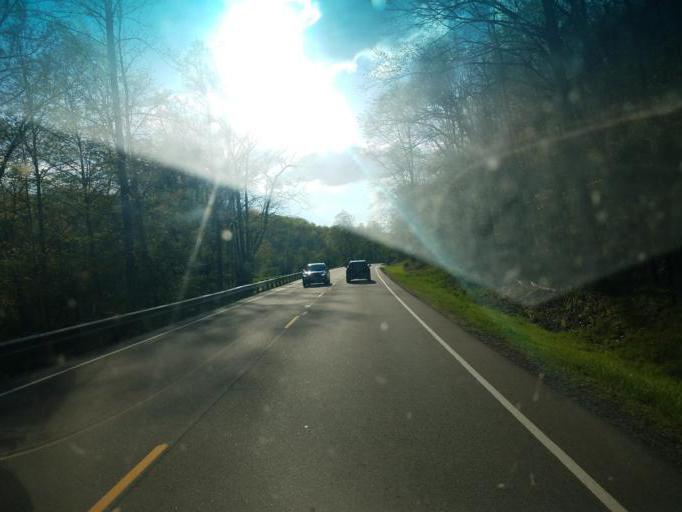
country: US
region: Ohio
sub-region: Knox County
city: Oak Hill
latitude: 40.3369
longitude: -82.0868
